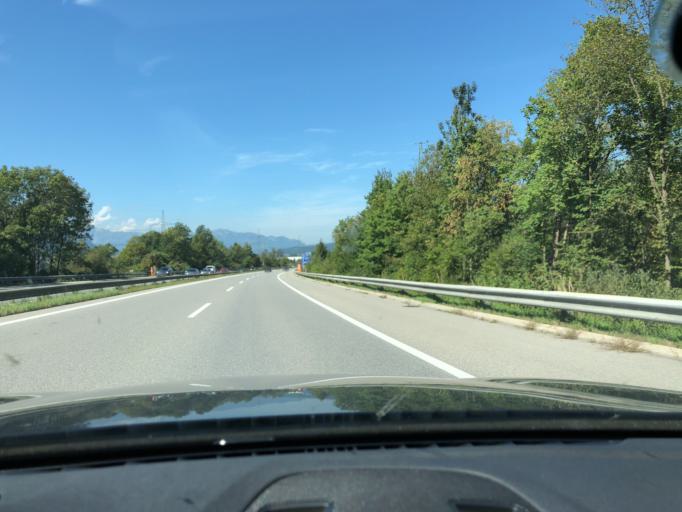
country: AT
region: Vorarlberg
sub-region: Politischer Bezirk Bludenz
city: Bludesch
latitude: 47.1789
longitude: 9.7318
